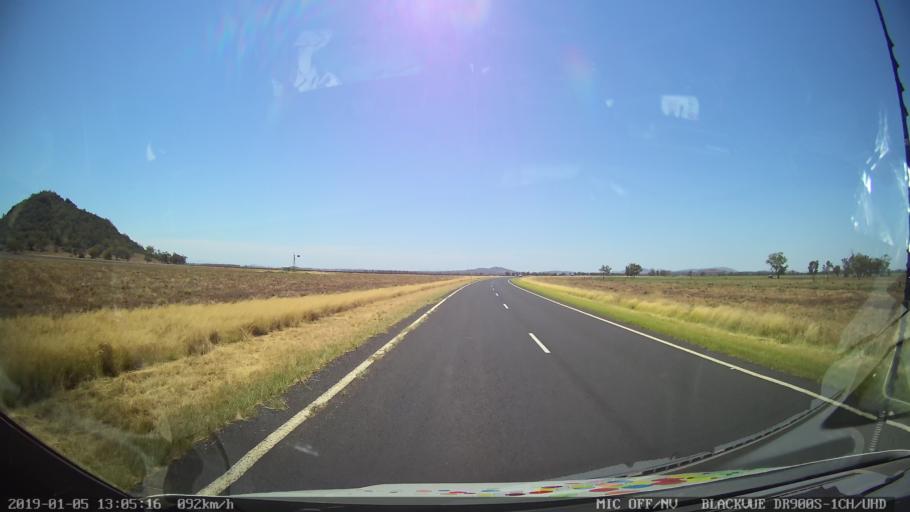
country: AU
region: New South Wales
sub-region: Gunnedah
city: Gunnedah
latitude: -31.0968
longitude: 149.8507
